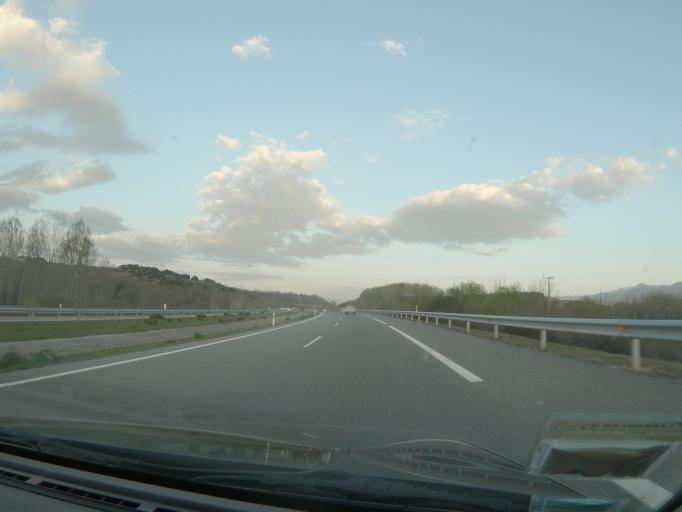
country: ES
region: Castille and Leon
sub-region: Provincia de Leon
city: Villadecanes
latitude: 42.5730
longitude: -6.7679
